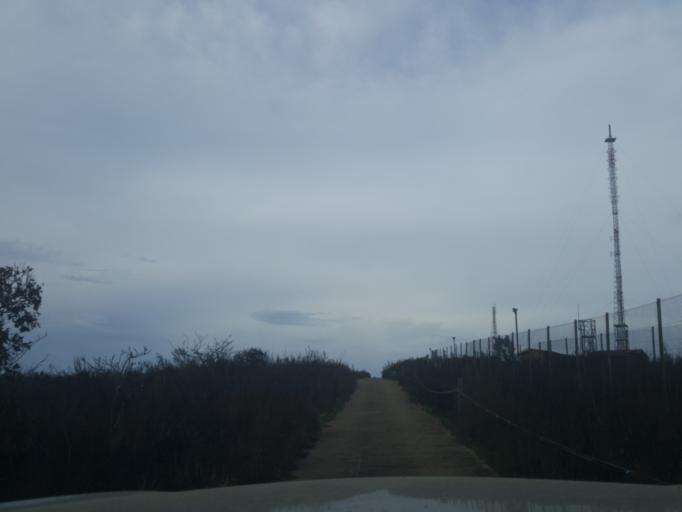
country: ZA
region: Limpopo
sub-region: Mopani District Municipality
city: Hoedspruit
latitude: -24.5453
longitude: 30.8656
